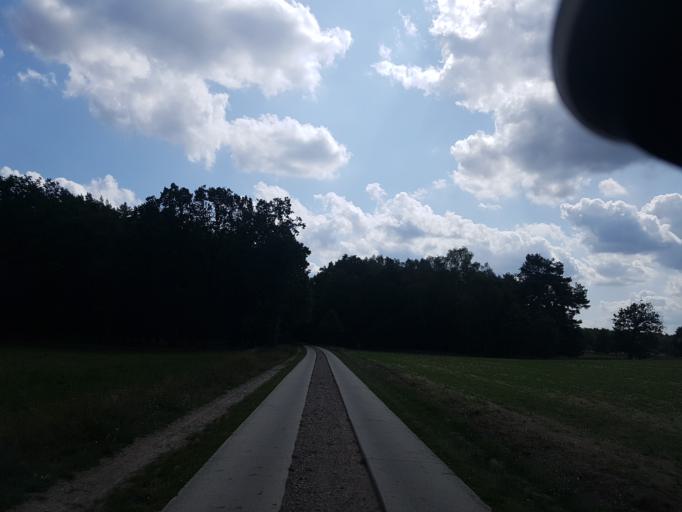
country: DE
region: Brandenburg
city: Borkwalde
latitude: 52.3095
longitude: 12.7844
